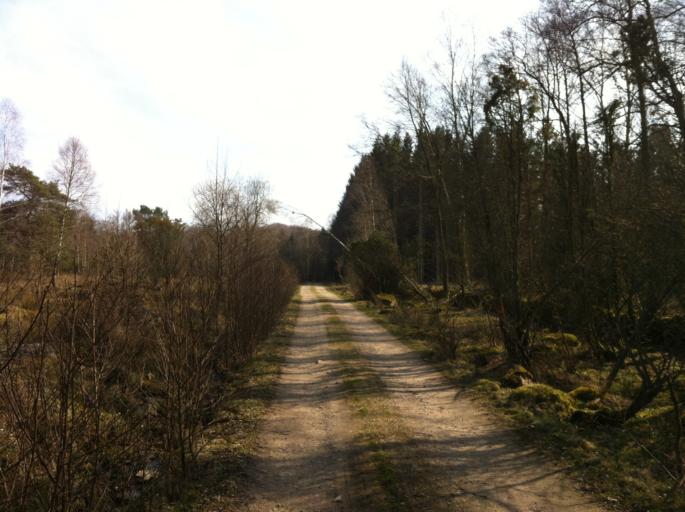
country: SE
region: Skane
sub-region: Eslovs Kommun
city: Stehag
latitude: 56.0126
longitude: 13.3664
